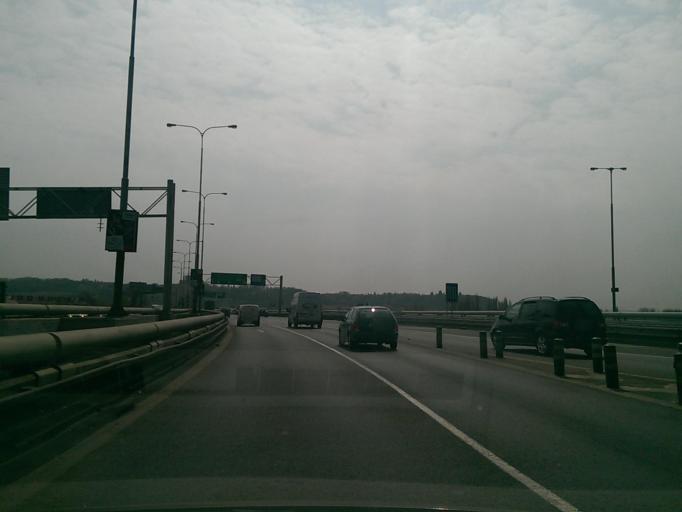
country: CZ
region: Praha
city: Branik
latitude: 50.0402
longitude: 14.4063
